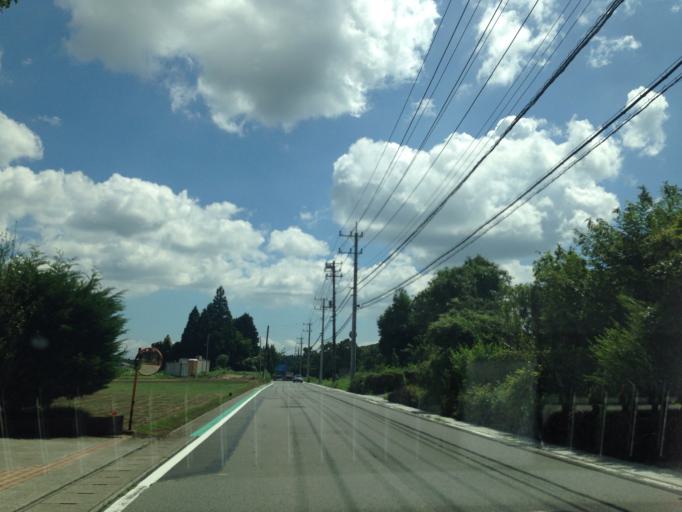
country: JP
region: Shizuoka
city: Gotemba
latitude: 35.2330
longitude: 138.8776
